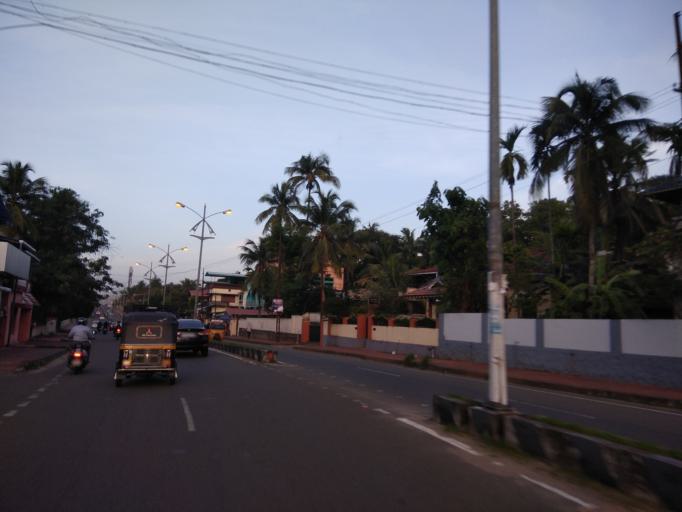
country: IN
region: Kerala
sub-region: Thrissur District
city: Trichur
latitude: 10.5211
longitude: 76.1928
